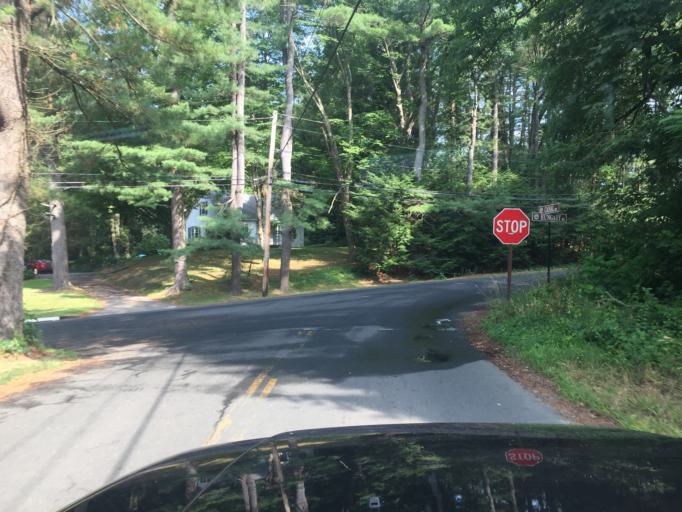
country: US
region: Connecticut
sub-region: Hartford County
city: Salmon Brook
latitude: 41.9585
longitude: -72.7834
